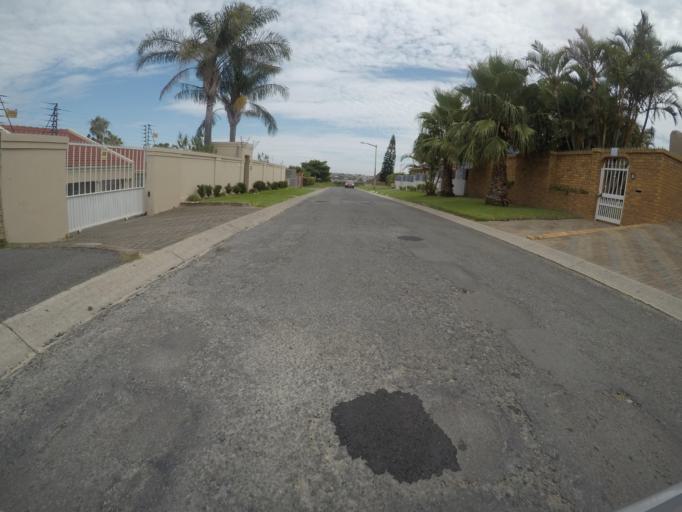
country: ZA
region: Eastern Cape
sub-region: Buffalo City Metropolitan Municipality
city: East London
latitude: -33.0011
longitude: 27.8821
